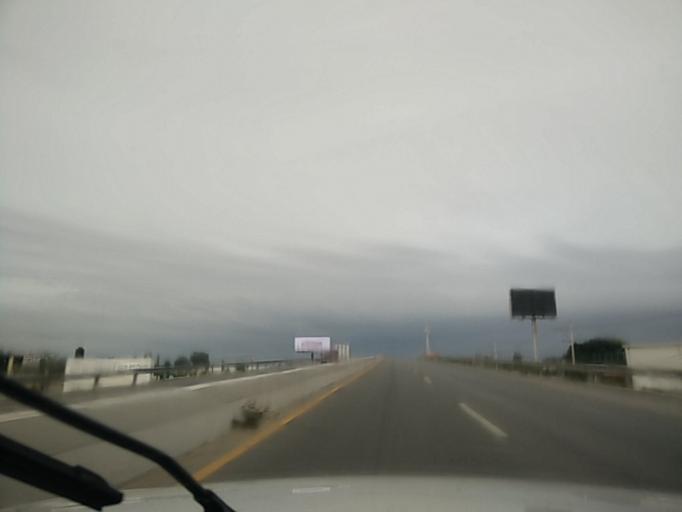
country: MX
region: Yucatan
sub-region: Kanasin
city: Kanasin
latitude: 20.9476
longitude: -89.5560
